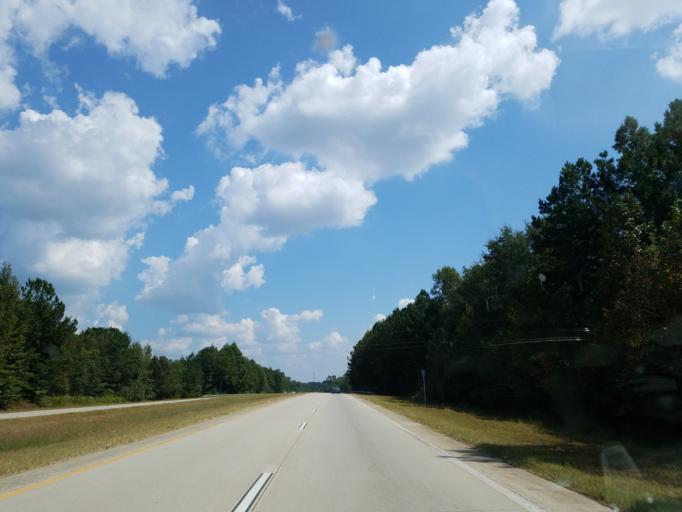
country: US
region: Georgia
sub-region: Oconee County
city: Bogart
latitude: 33.9197
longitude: -83.4945
